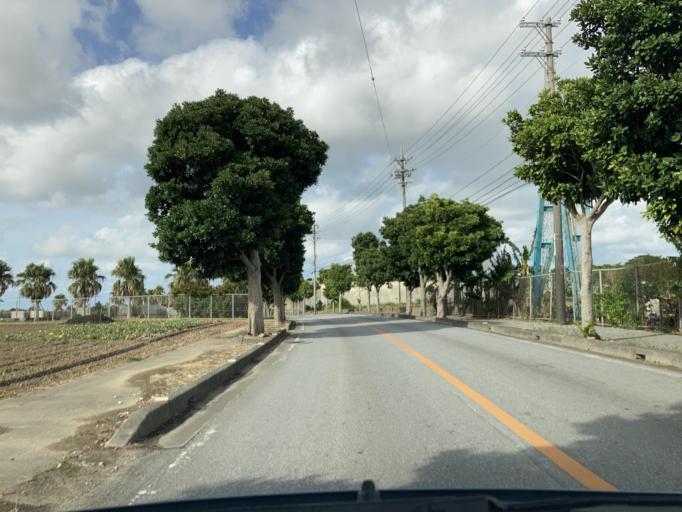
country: JP
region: Okinawa
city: Itoman
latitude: 26.1207
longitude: 127.7150
